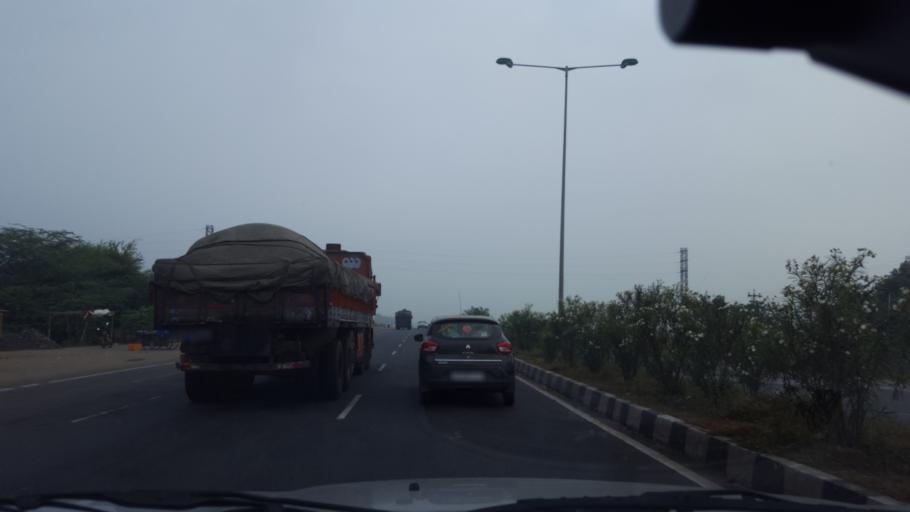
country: IN
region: Andhra Pradesh
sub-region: Prakasam
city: Ongole
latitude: 15.6379
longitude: 80.0162
